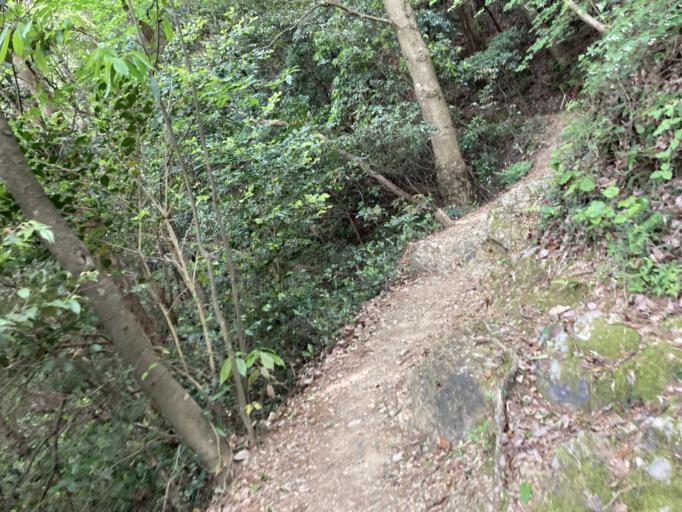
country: JP
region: Shizuoka
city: Kosai-shi
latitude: 34.7445
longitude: 137.4588
